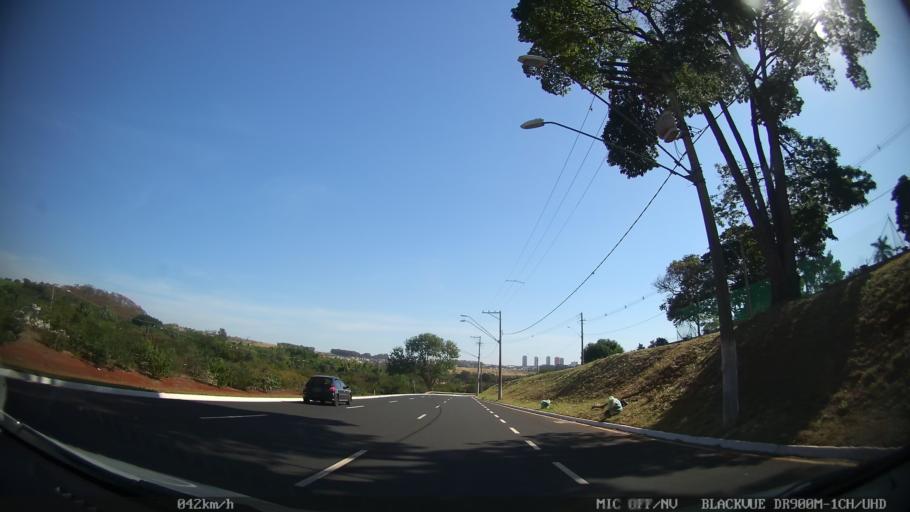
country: BR
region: Sao Paulo
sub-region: Ribeirao Preto
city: Ribeirao Preto
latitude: -21.2376
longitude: -47.7613
